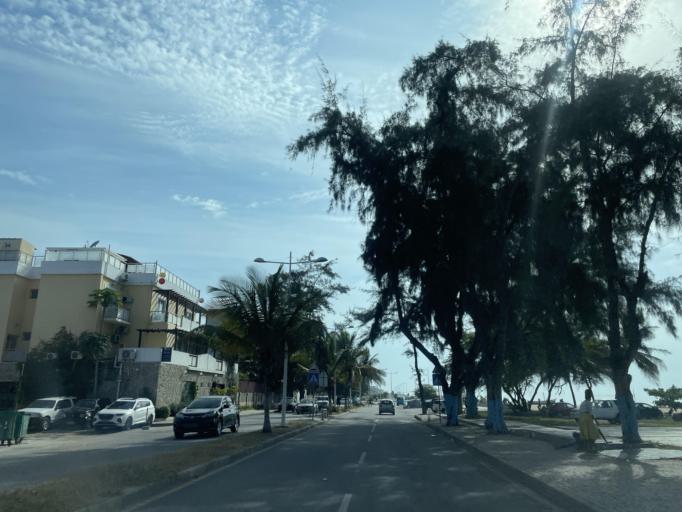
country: AO
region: Luanda
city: Luanda
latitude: -8.7693
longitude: 13.2535
